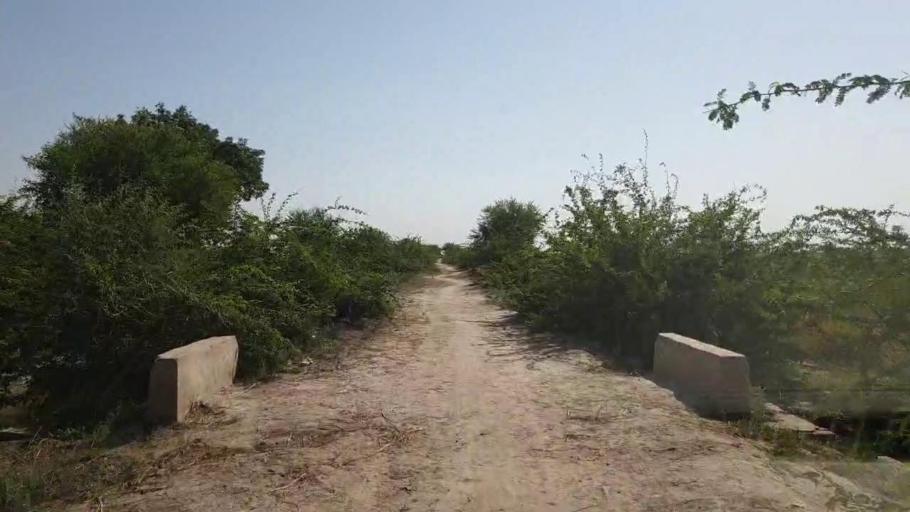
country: PK
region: Sindh
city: Kadhan
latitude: 24.5992
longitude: 69.0048
